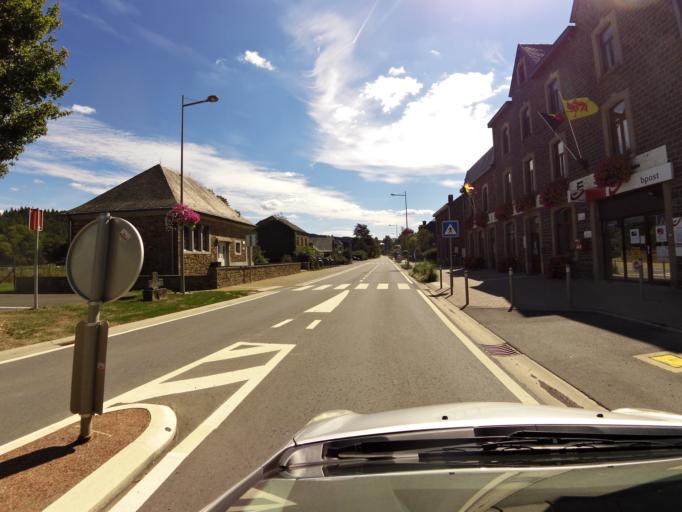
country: BE
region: Wallonia
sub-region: Province du Luxembourg
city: Rendeux
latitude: 50.2350
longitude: 5.5095
